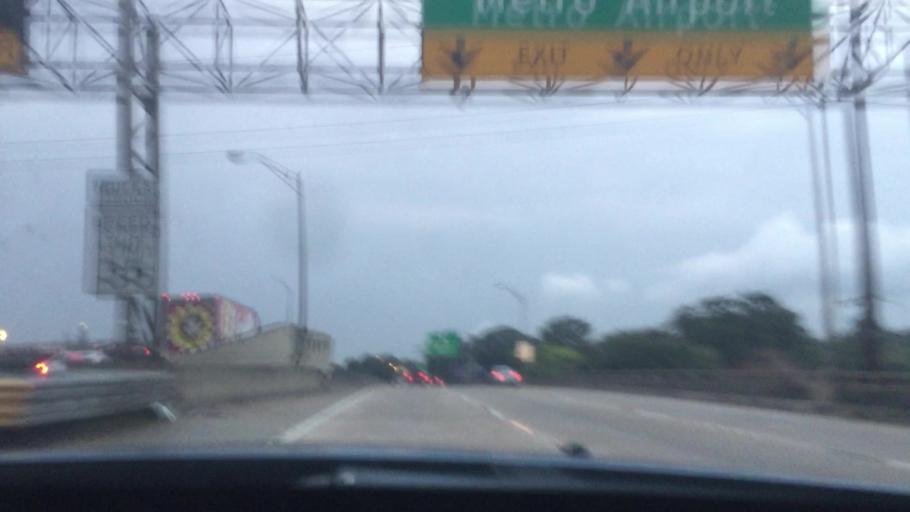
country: US
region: Louisiana
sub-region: East Baton Rouge Parish
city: Baton Rouge
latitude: 30.4372
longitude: -91.1778
